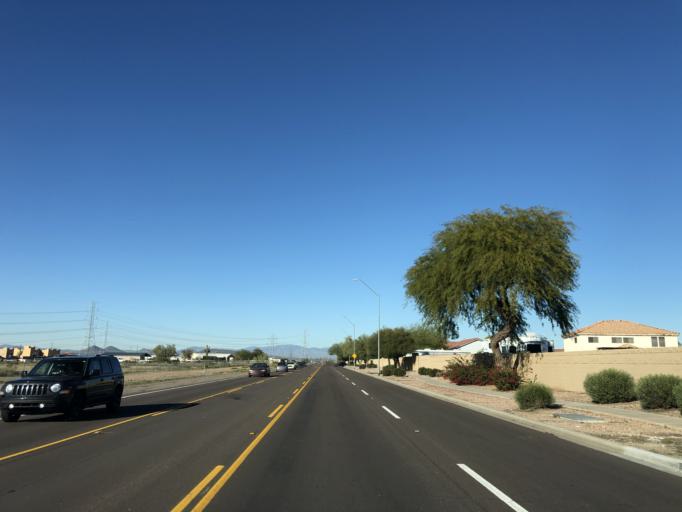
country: US
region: Arizona
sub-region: Maricopa County
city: Sun City West
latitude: 33.6908
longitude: -112.2897
